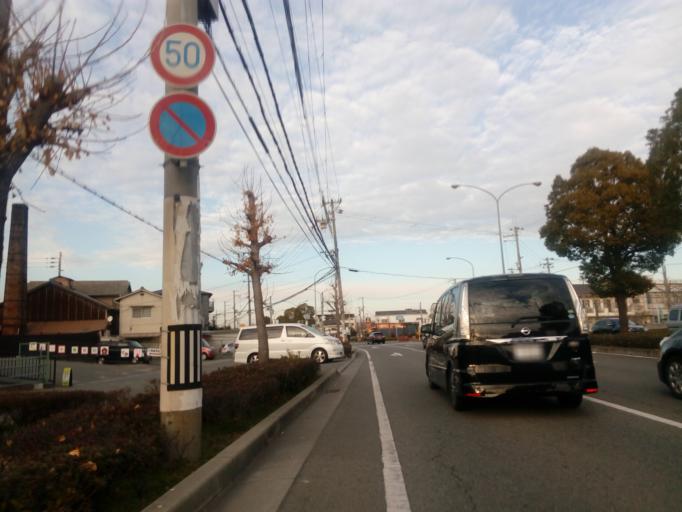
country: JP
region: Hyogo
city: Himeji
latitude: 34.7967
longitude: 134.6770
